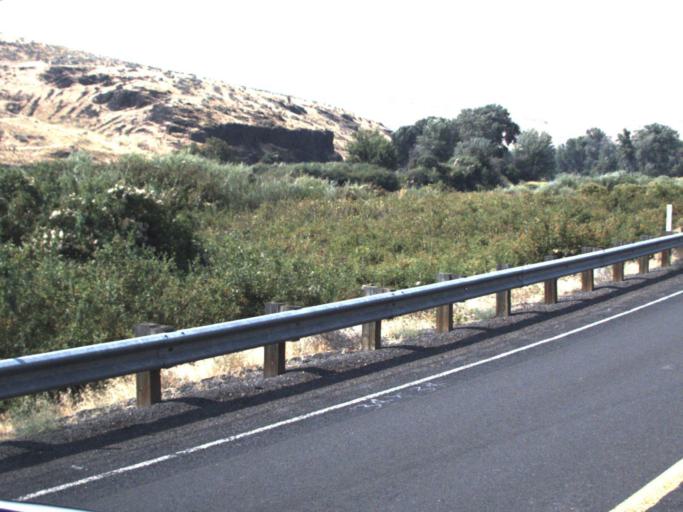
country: US
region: Washington
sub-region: Yakima County
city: Selah
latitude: 46.7724
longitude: -120.4483
